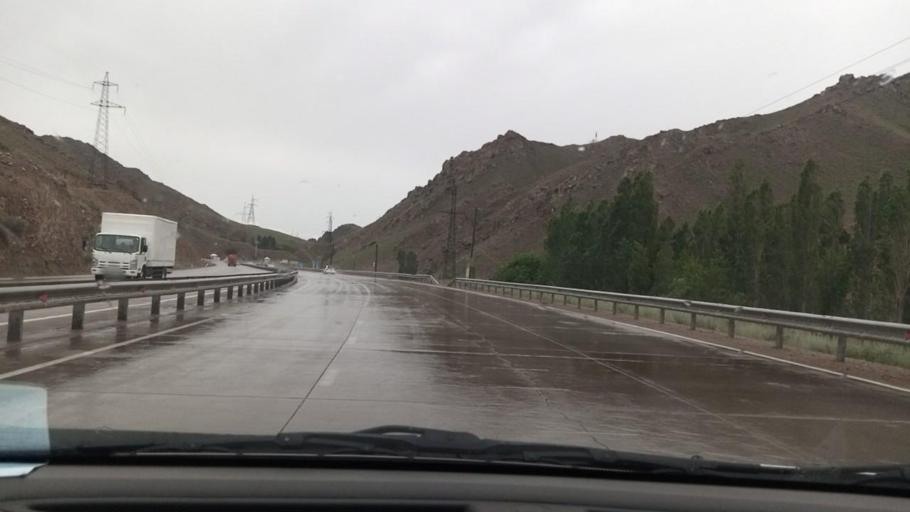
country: TJ
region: Viloyati Sughd
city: Shaydon
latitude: 40.9630
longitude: 70.6611
